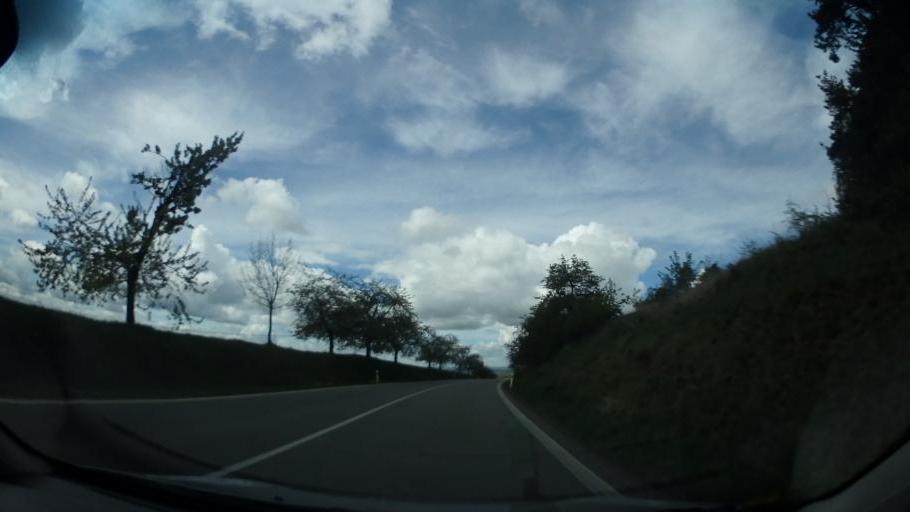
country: CZ
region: Vysocina
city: Krizanov
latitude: 49.3236
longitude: 16.1098
